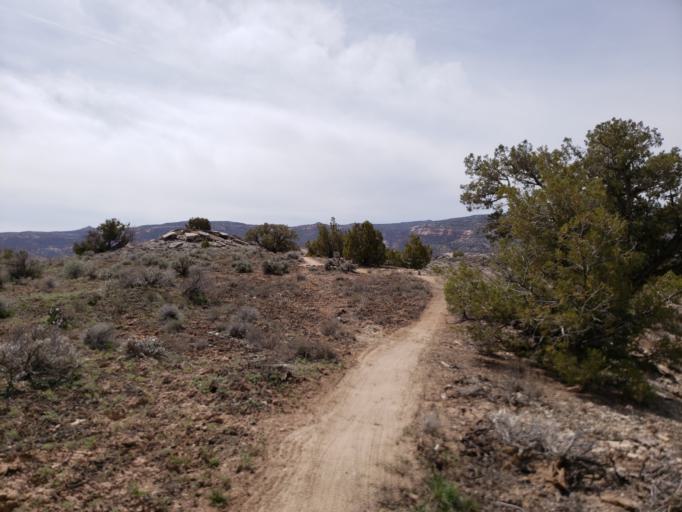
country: US
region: Colorado
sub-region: Mesa County
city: Loma
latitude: 39.1810
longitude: -108.8529
